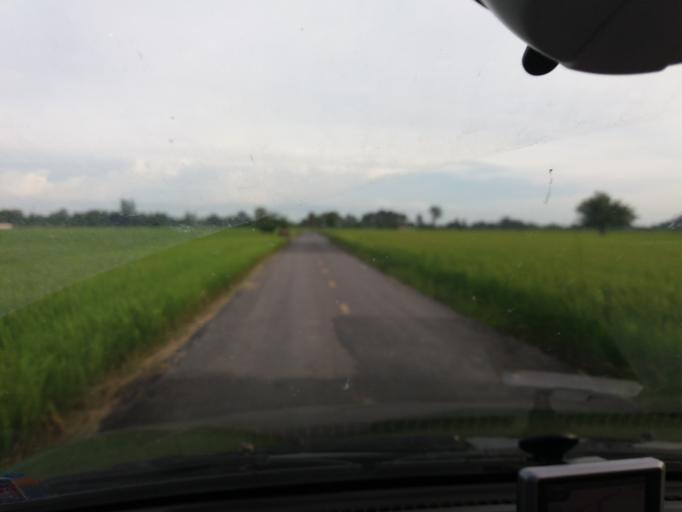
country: TH
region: Suphan Buri
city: Doembang Nangbuat
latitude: 14.8273
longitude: 100.1425
